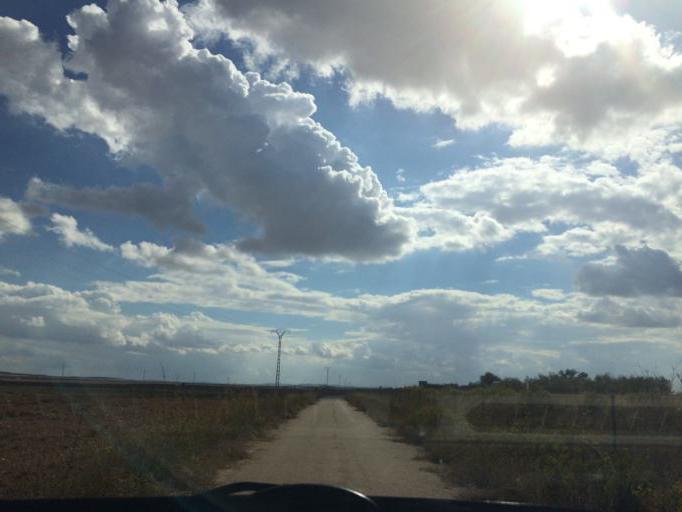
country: ES
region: Castille-La Mancha
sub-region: Provincia de Albacete
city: Albacete
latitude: 38.9568
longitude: -1.8215
